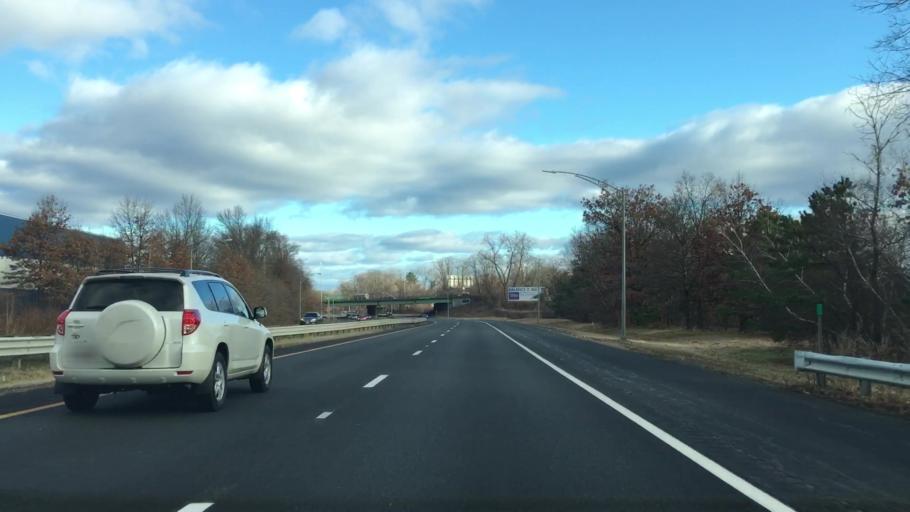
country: US
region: Massachusetts
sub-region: Hampden County
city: Springfield
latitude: 42.1399
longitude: -72.5523
